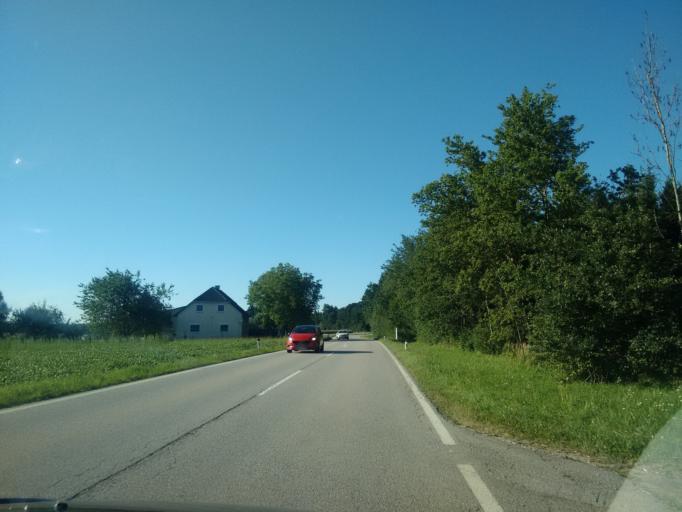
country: AT
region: Upper Austria
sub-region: Wels-Land
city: Sattledt
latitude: 48.1142
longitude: 14.0964
